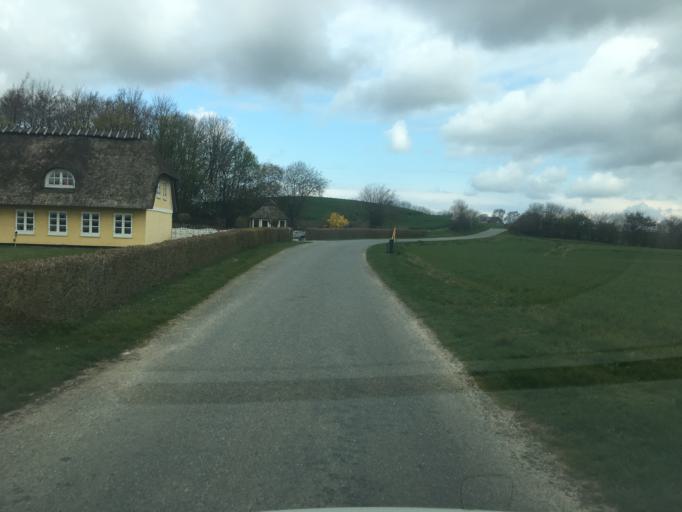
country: DK
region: South Denmark
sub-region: Sonderborg Kommune
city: Grasten
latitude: 54.9881
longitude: 9.5233
